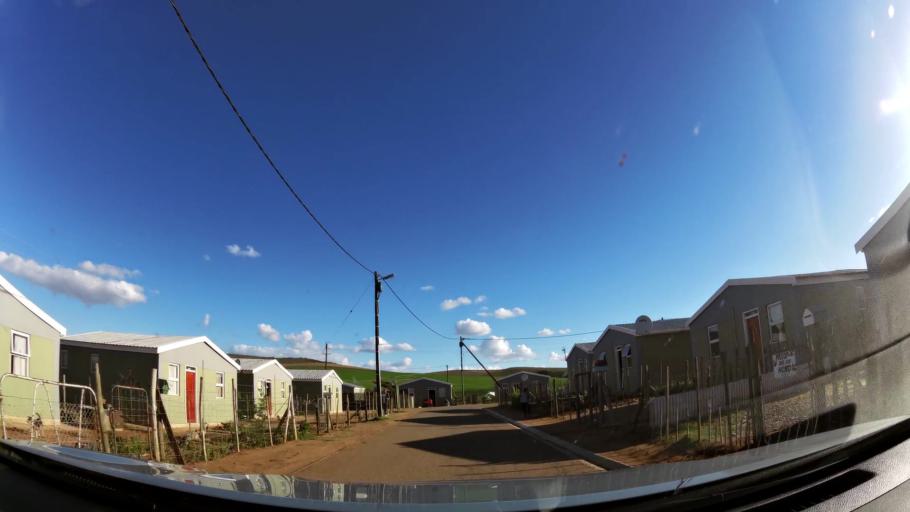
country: ZA
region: Western Cape
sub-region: Eden District Municipality
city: Riversdale
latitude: -34.1109
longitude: 20.9641
